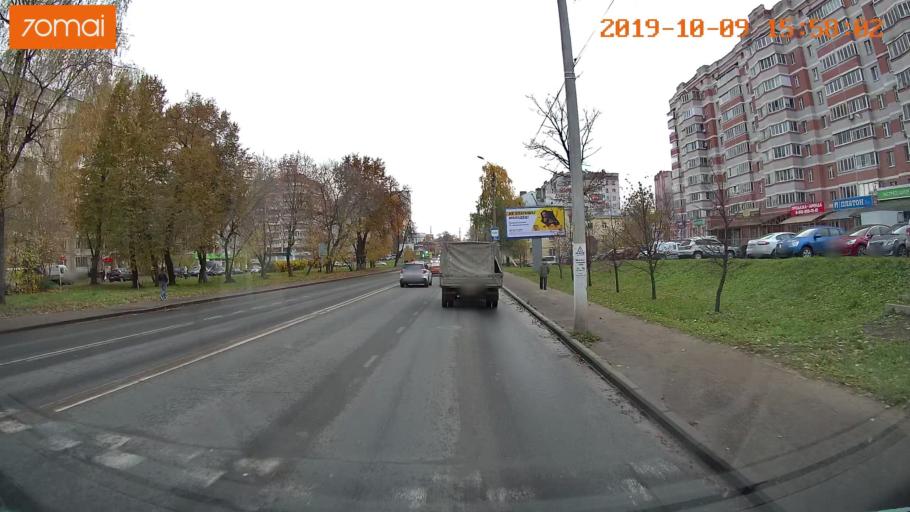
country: RU
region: Kostroma
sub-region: Kostromskoy Rayon
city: Kostroma
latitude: 57.7683
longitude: 40.9508
